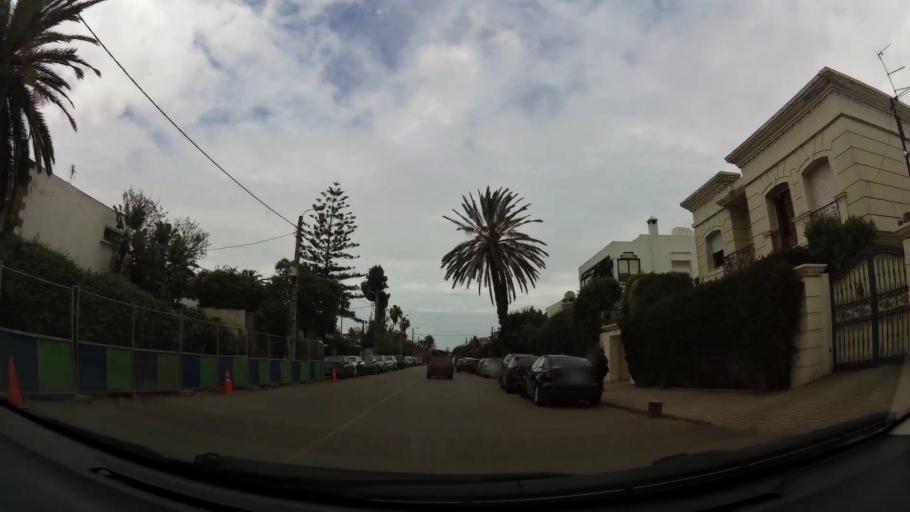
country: MA
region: Grand Casablanca
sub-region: Casablanca
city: Casablanca
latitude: 33.5730
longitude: -7.6581
